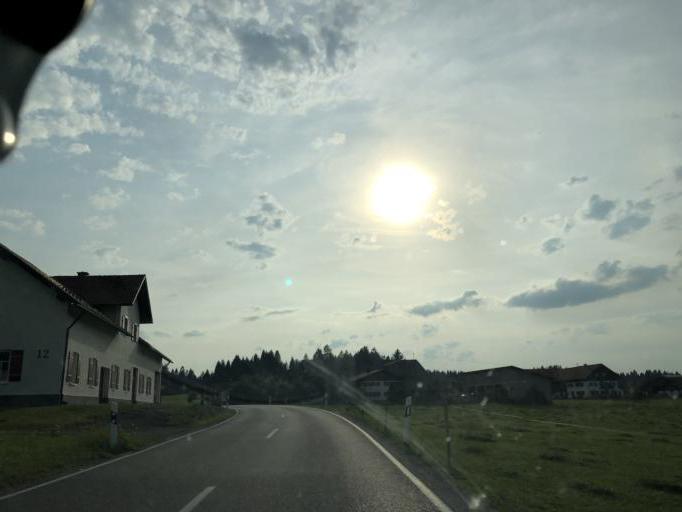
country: DE
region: Bavaria
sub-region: Swabia
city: Gorisried
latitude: 47.7029
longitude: 10.4917
